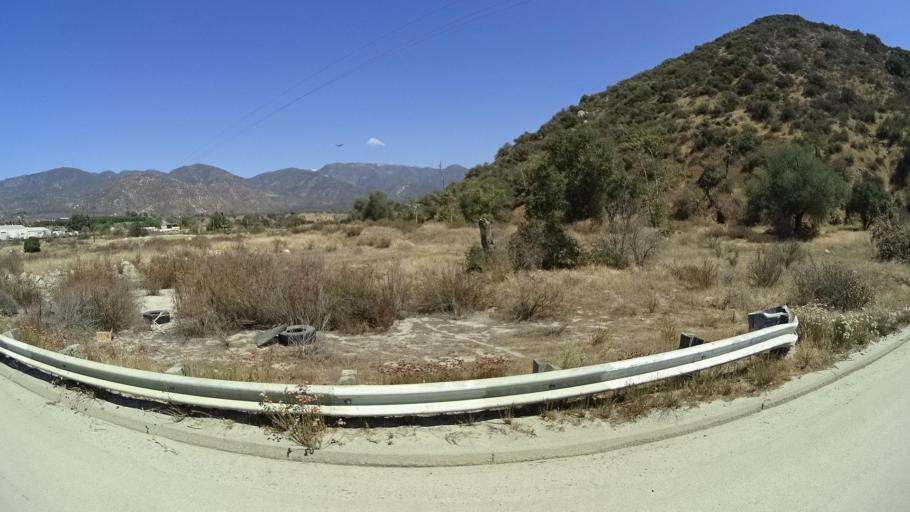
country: US
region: California
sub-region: San Diego County
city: Rainbow
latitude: 33.3607
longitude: -117.0625
